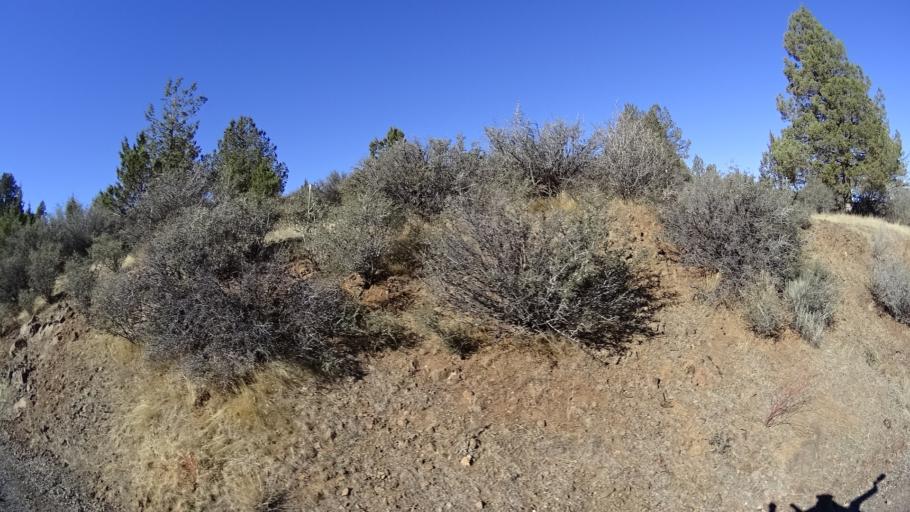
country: US
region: California
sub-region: Siskiyou County
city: Montague
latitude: 41.9120
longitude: -122.3724
